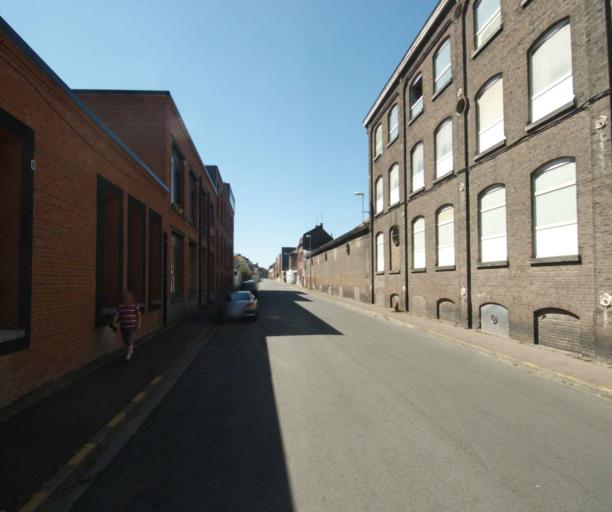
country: FR
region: Nord-Pas-de-Calais
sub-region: Departement du Nord
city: Tourcoing
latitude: 50.7223
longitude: 3.1758
